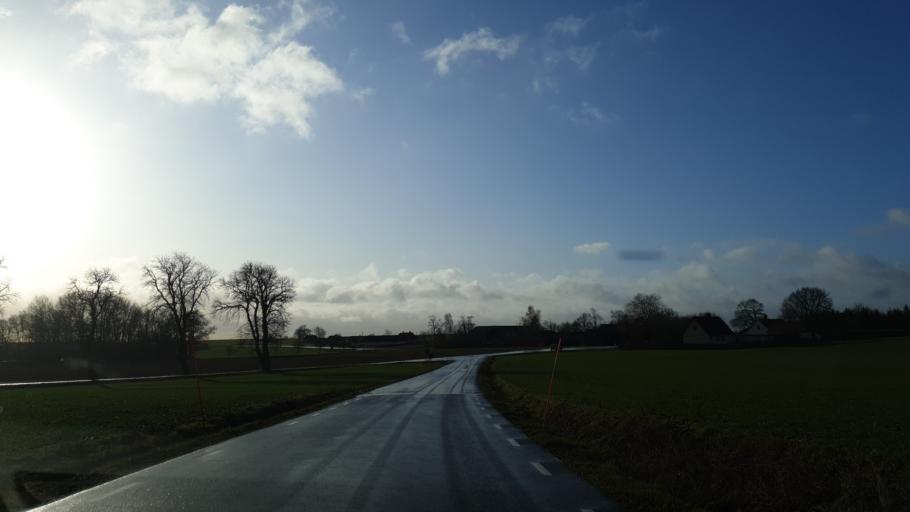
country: SE
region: Skane
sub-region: Skurups Kommun
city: Rydsgard
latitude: 55.4526
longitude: 13.5497
